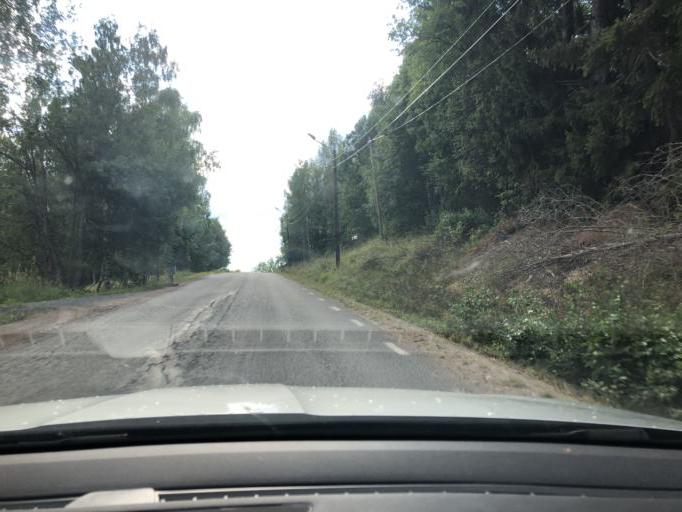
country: SE
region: Vaesternorrland
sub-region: Solleftea Kommun
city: Solleftea
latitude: 63.2105
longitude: 17.1710
